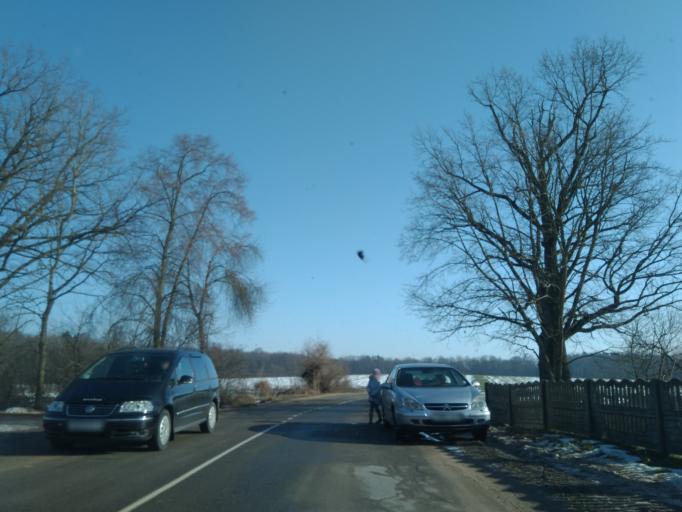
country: BY
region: Minsk
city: Nyasvizh
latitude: 53.2030
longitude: 26.6476
